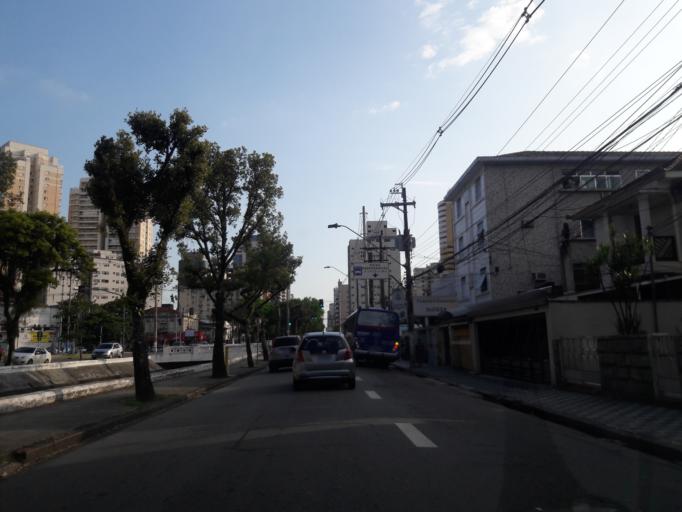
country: BR
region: Sao Paulo
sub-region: Santos
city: Santos
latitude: -23.9606
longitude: -46.3383
